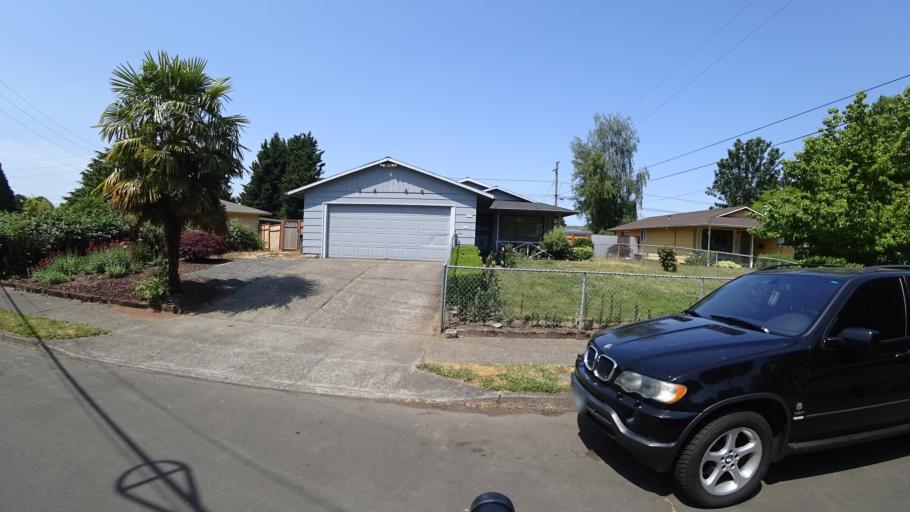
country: US
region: Washington
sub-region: Clark County
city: Vancouver
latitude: 45.5871
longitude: -122.7036
